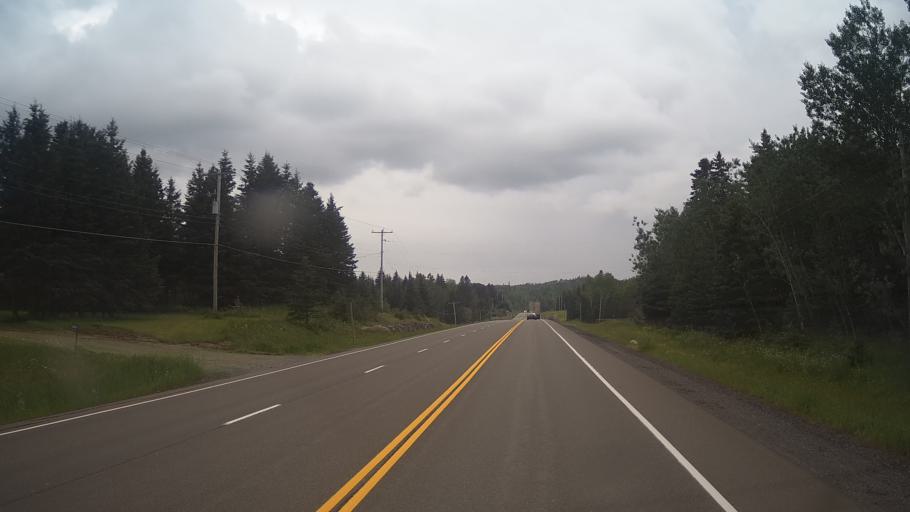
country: CA
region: Ontario
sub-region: Thunder Bay District
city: Thunder Bay
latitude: 48.5253
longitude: -89.5247
